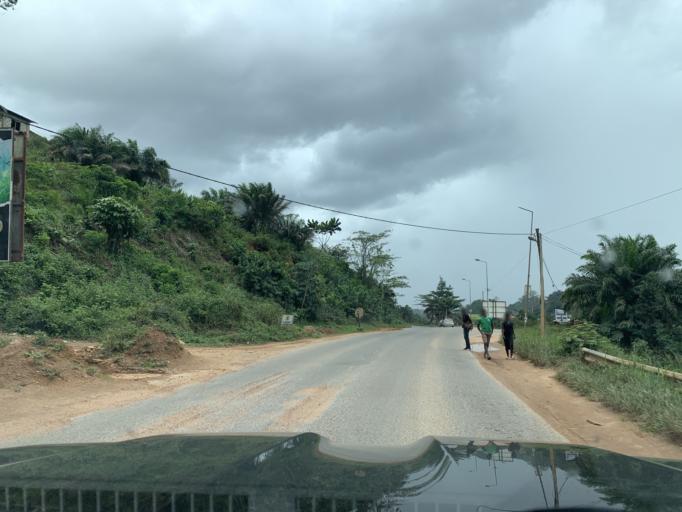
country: GH
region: Western
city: Tarkwa
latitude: 5.3219
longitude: -1.9850
